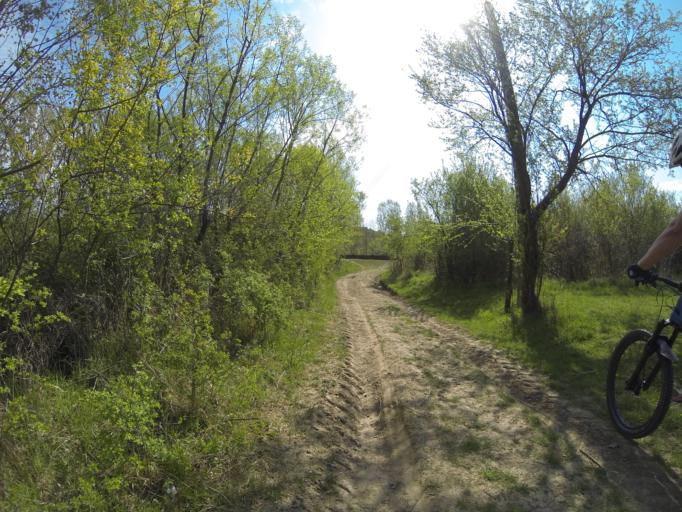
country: RO
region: Dolj
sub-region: Comuna Bradesti
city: Bradesti
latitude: 44.5301
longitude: 23.6252
